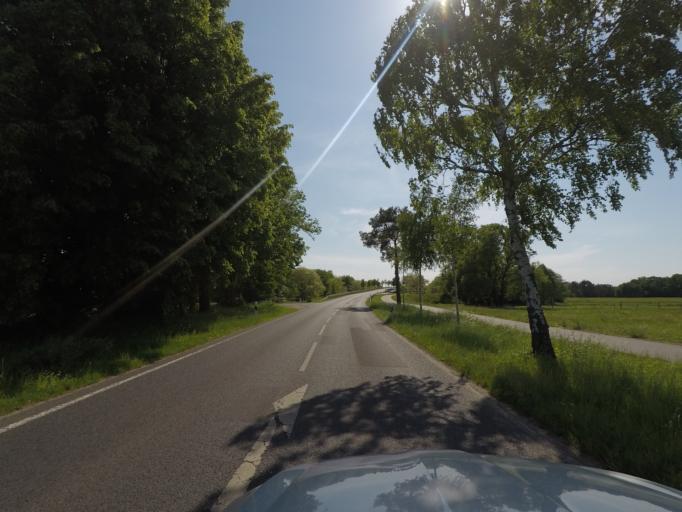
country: DE
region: Brandenburg
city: Britz
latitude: 52.8585
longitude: 13.7400
